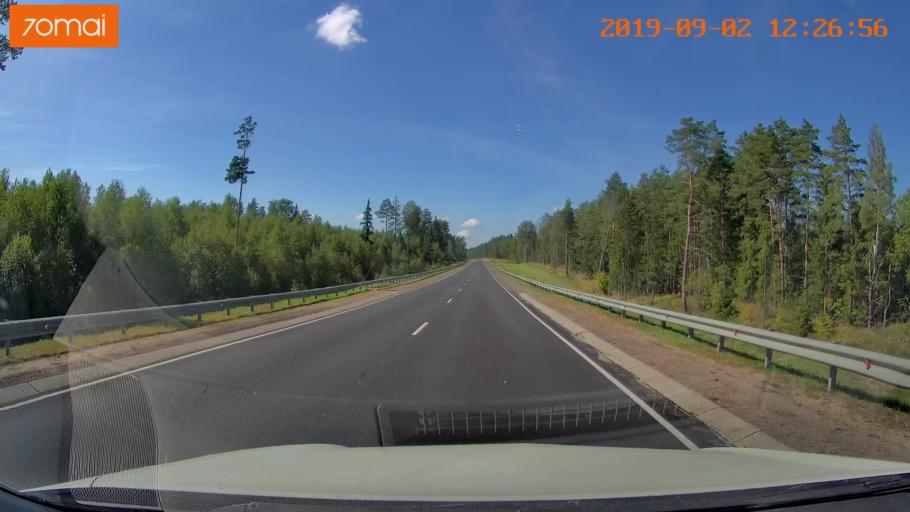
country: RU
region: Smolensk
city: Shumyachi
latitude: 53.8551
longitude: 32.5568
